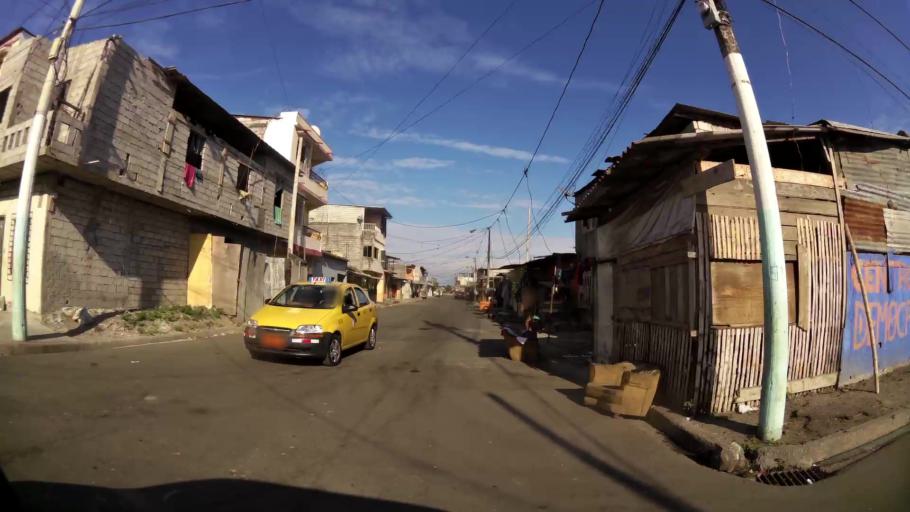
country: EC
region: Guayas
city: Guayaquil
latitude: -2.2214
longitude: -79.9176
